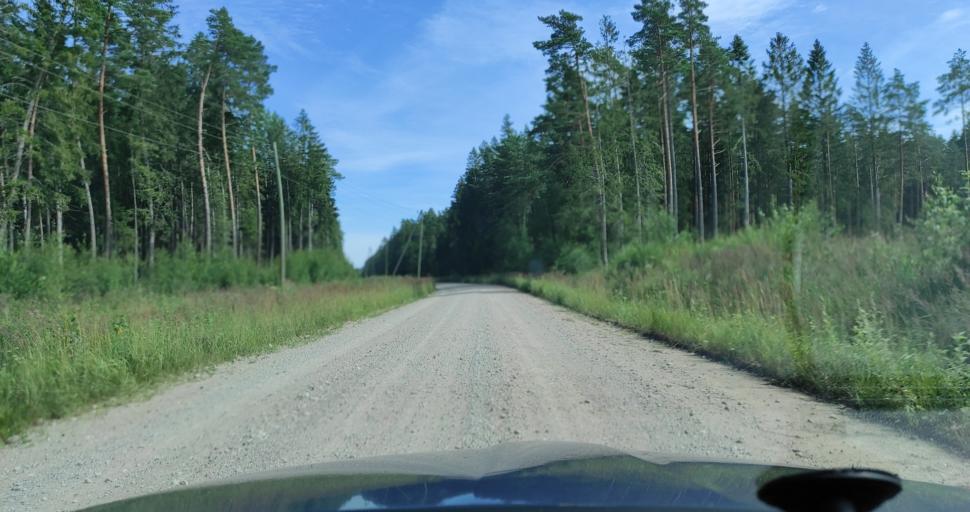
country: LV
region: Durbe
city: Liegi
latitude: 56.7549
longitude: 21.3390
